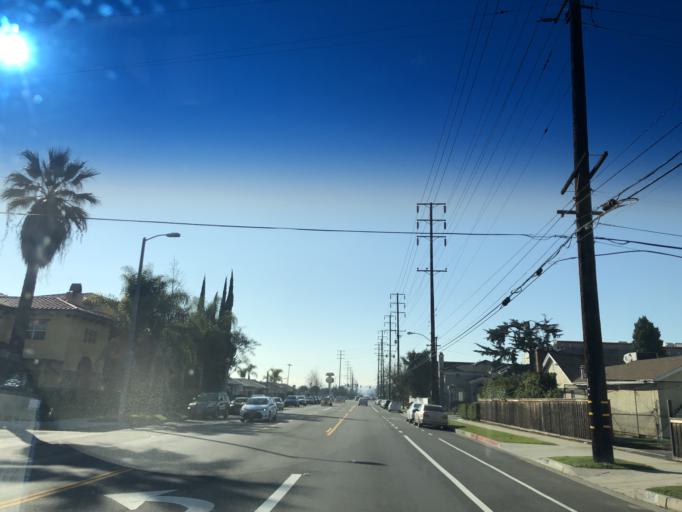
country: US
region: California
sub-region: Los Angeles County
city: East San Gabriel
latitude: 34.0823
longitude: -118.0996
